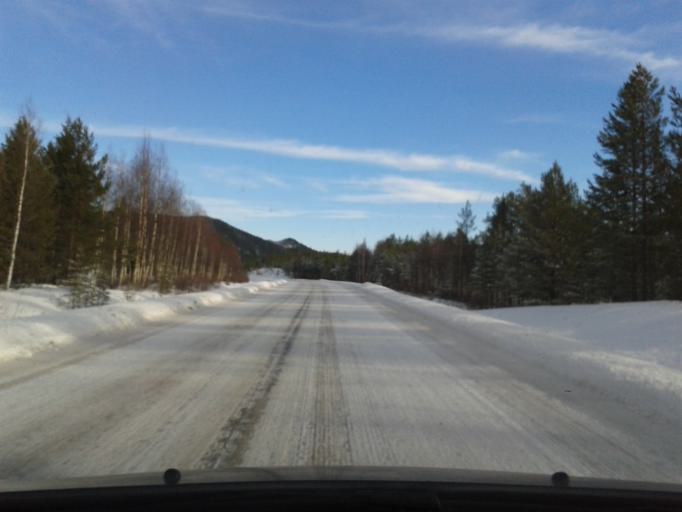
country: SE
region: Vaesterbotten
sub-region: Asele Kommun
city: Asele
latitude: 64.3154
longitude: 17.1772
